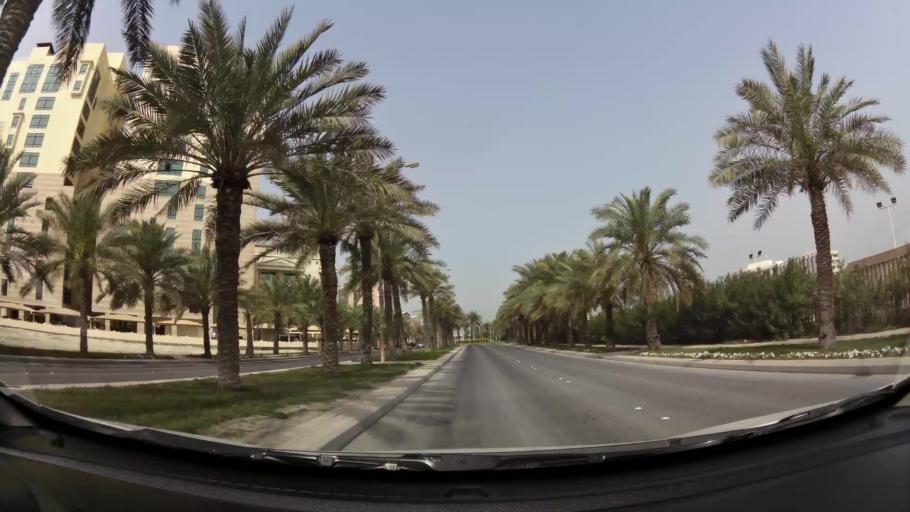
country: BH
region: Manama
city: Jidd Hafs
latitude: 26.2412
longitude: 50.5394
